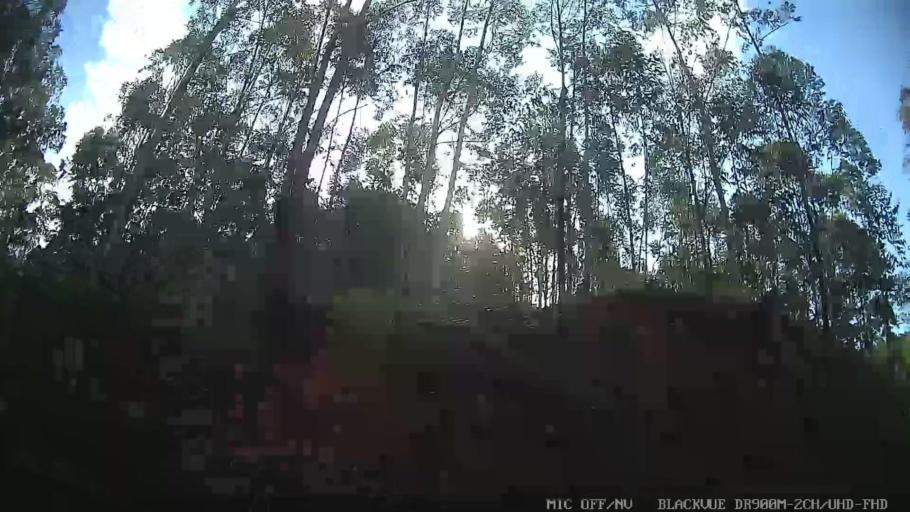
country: BR
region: Sao Paulo
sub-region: Serra Negra
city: Serra Negra
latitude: -22.6632
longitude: -46.6889
